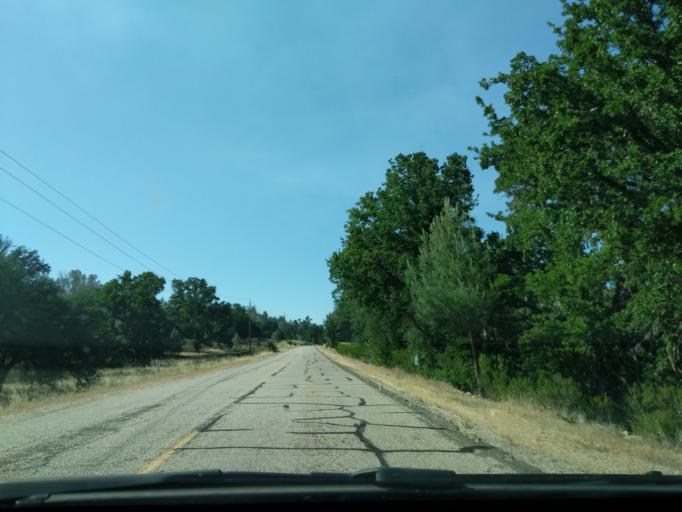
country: US
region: California
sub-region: Monterey County
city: King City
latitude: 35.9793
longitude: -121.1769
